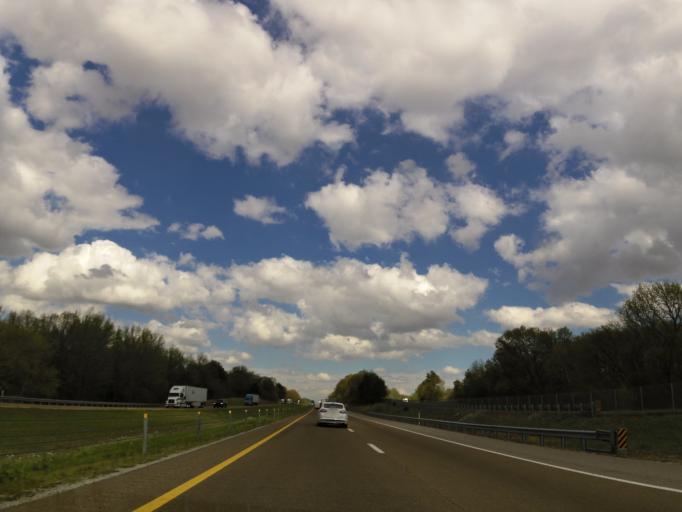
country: US
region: Tennessee
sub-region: Crockett County
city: Bells
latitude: 35.6115
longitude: -89.0174
